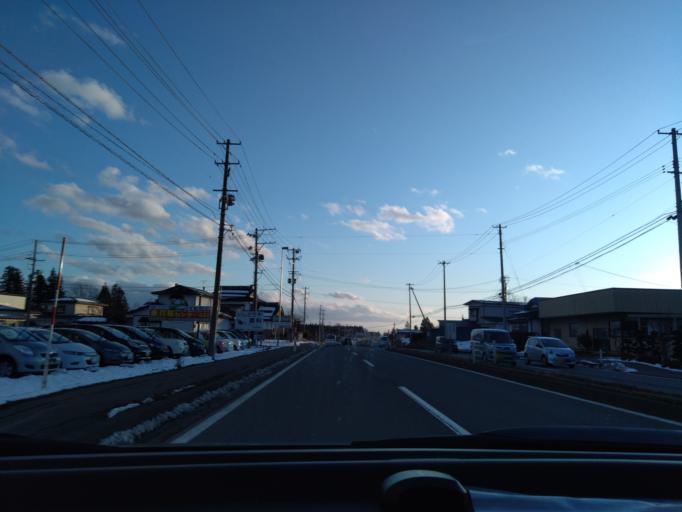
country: JP
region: Iwate
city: Hanamaki
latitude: 39.5252
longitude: 141.1625
